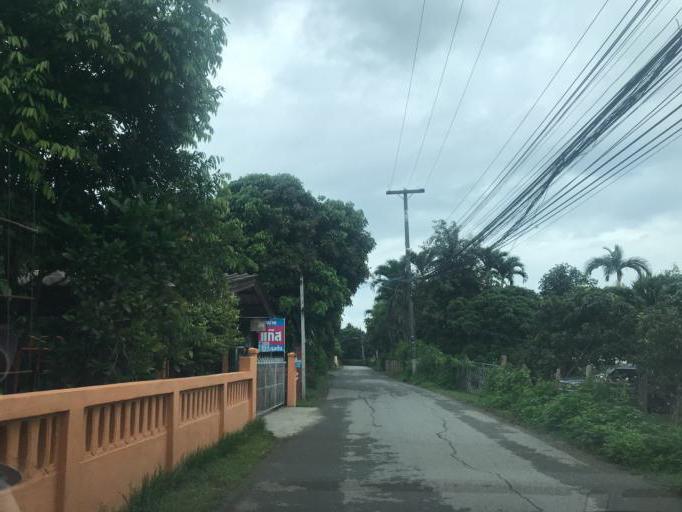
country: TH
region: Chiang Mai
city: Saraphi
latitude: 18.6992
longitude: 99.0223
